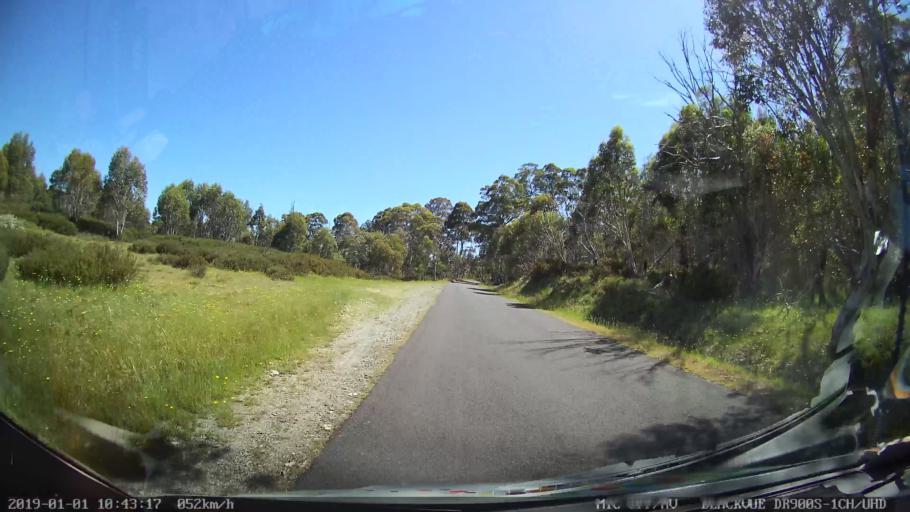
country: AU
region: New South Wales
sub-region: Snowy River
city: Jindabyne
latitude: -36.0369
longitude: 148.3238
